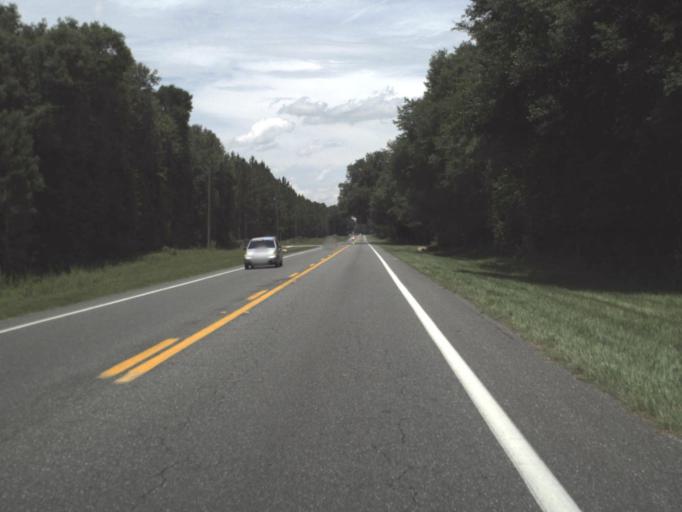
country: US
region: Florida
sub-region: Suwannee County
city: Live Oak
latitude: 30.2705
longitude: -83.0187
